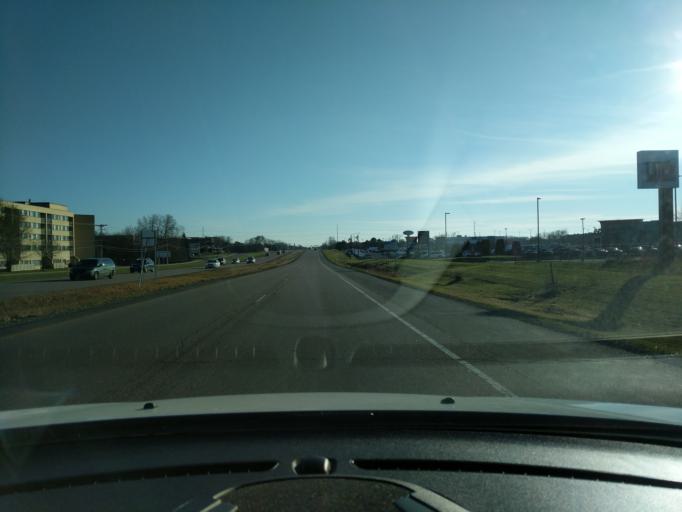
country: US
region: Minnesota
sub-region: Ramsey County
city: Roseville
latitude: 45.0274
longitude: -93.1673
